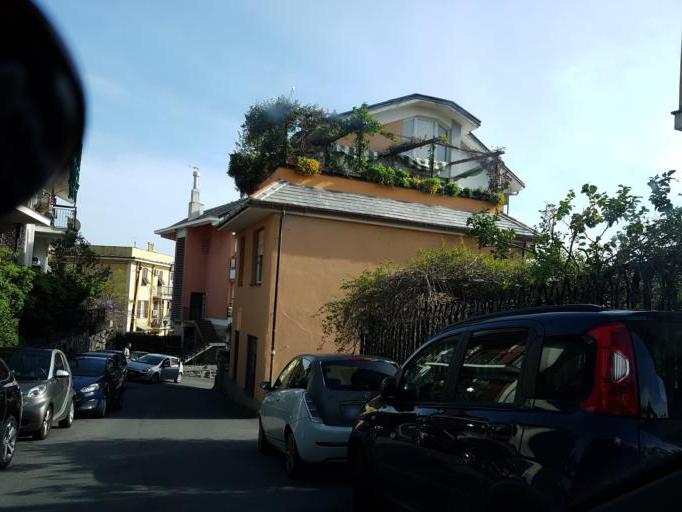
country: IT
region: Liguria
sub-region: Provincia di Genova
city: Bogliasco
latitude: 44.3907
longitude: 9.0128
